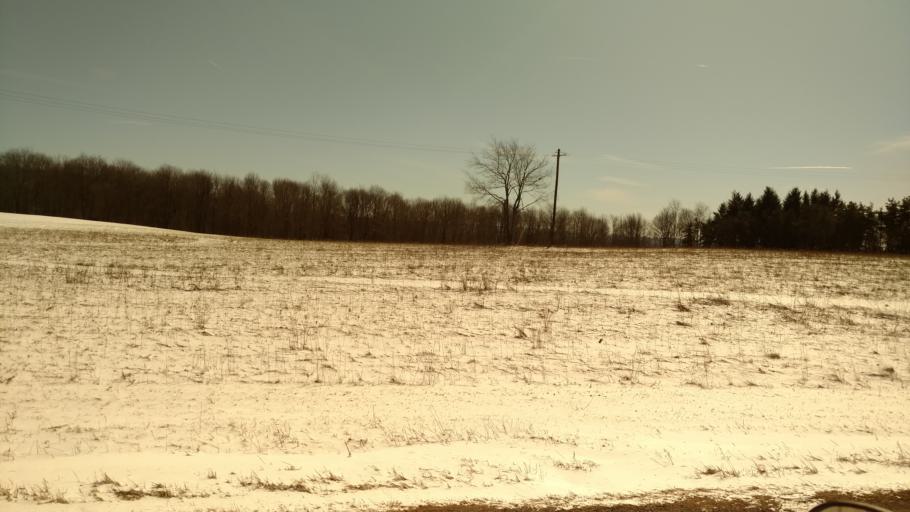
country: US
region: New York
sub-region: Allegany County
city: Wellsville
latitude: 42.0567
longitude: -78.0087
